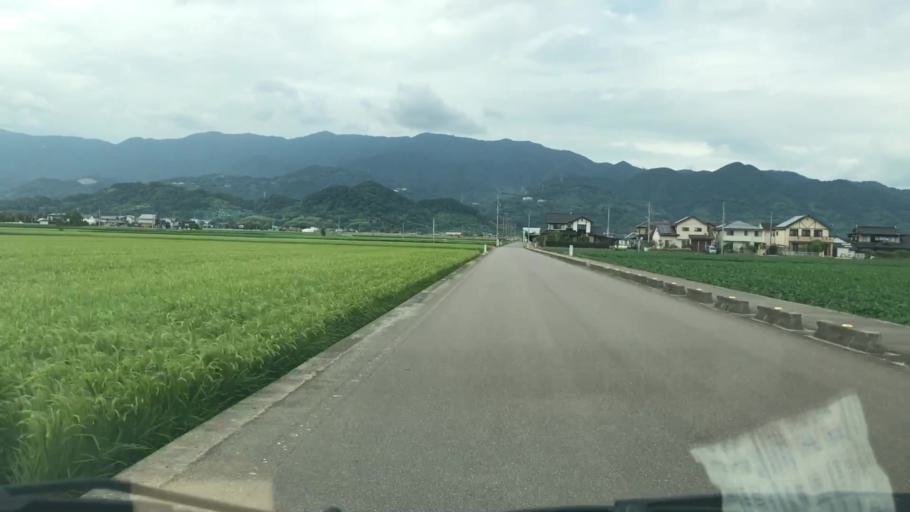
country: JP
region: Saga Prefecture
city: Saga-shi
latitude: 33.2840
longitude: 130.2258
